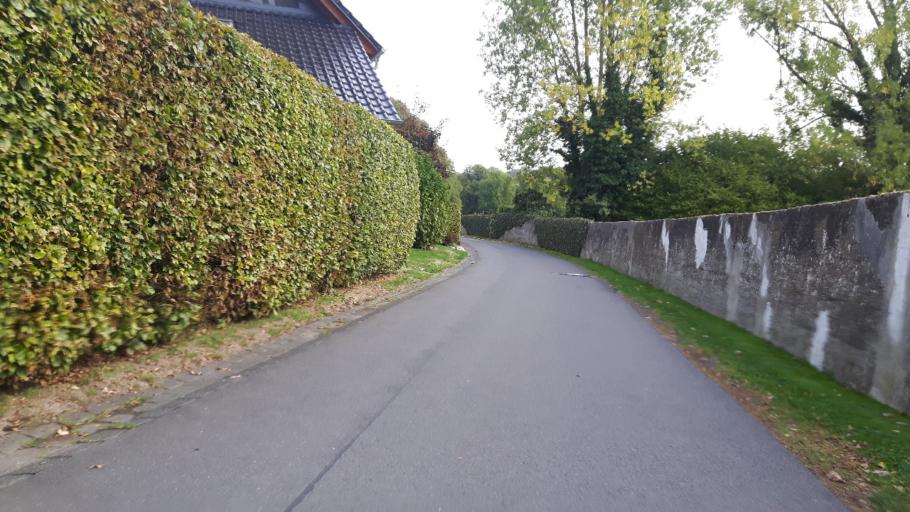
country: DE
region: North Rhine-Westphalia
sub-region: Regierungsbezirk Koln
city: Eitorf
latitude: 50.7676
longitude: 7.3930
